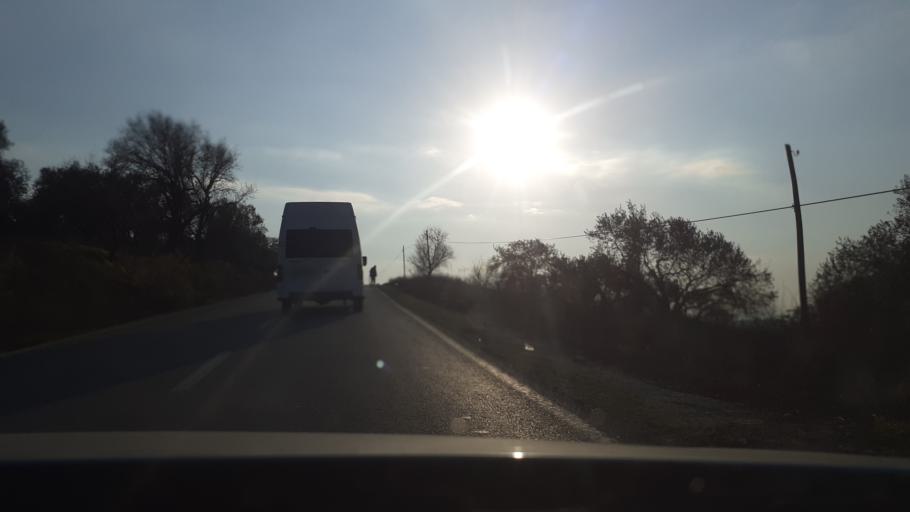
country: TR
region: Hatay
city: Oymakli
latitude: 36.1222
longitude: 36.3068
